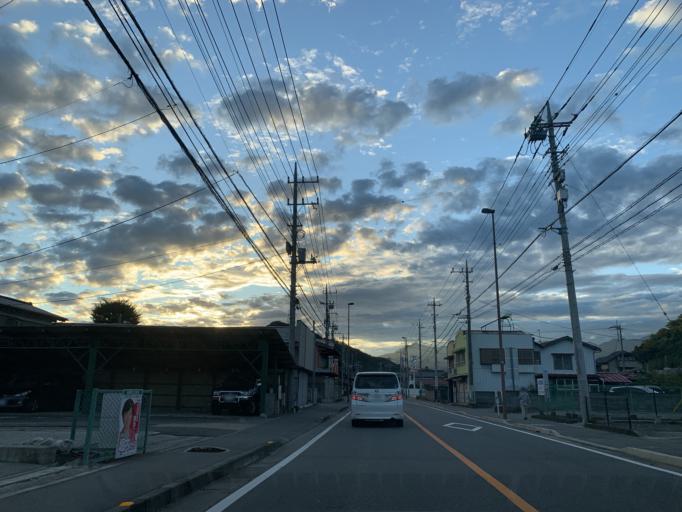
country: JP
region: Yamanashi
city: Otsuki
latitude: 35.6088
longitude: 139.0026
